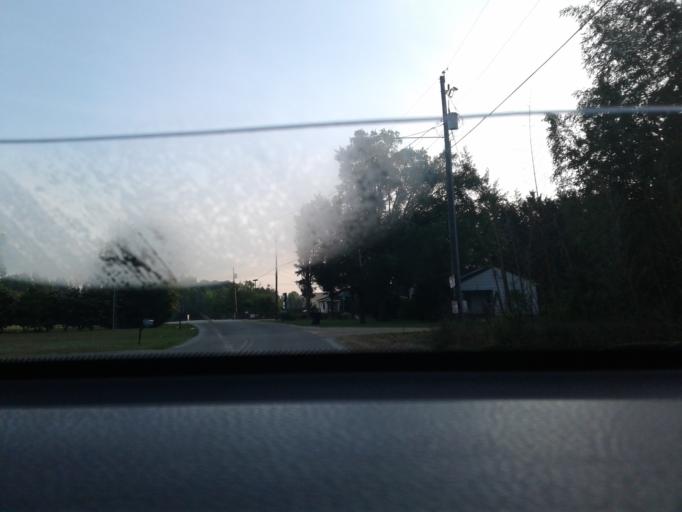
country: US
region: North Carolina
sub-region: Harnett County
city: Erwin
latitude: 35.3233
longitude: -78.6517
